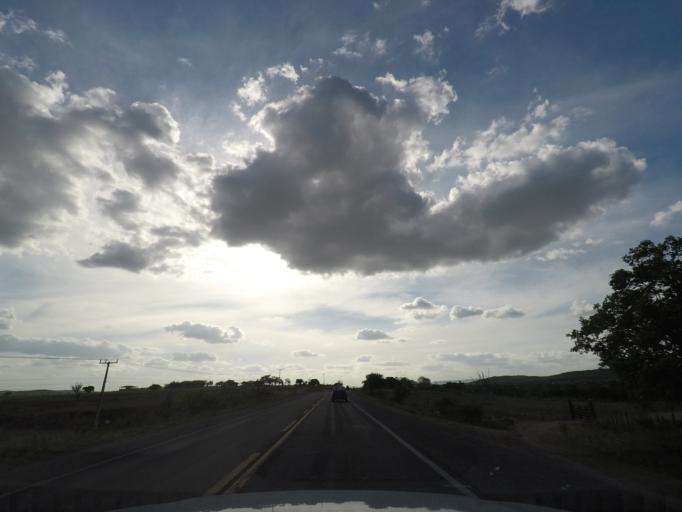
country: BR
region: Bahia
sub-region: Anguera
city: Anguera
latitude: -12.1866
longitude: -39.4864
